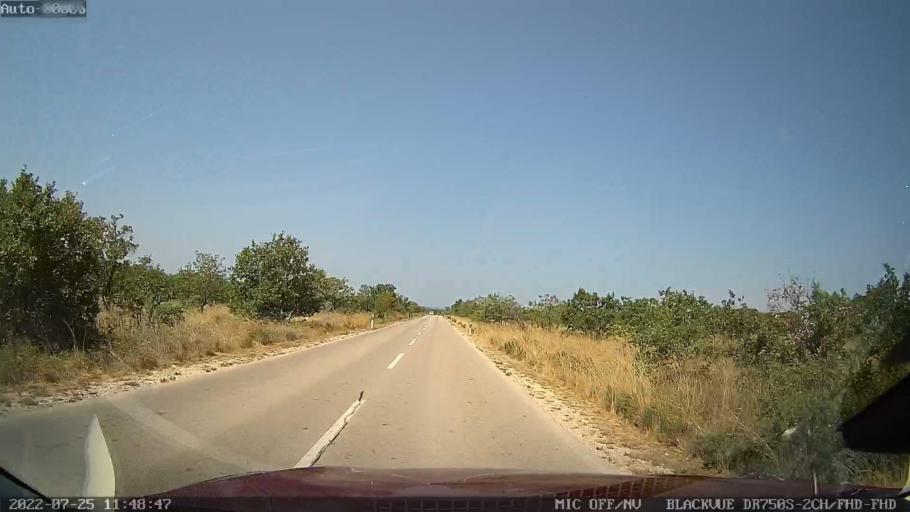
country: HR
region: Zadarska
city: Vrsi
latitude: 44.2344
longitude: 15.2931
